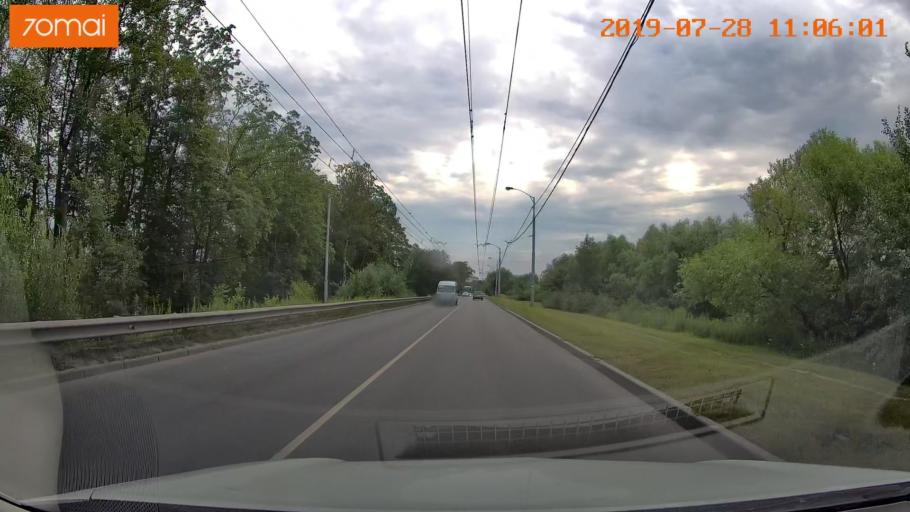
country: RU
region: Kaliningrad
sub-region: Gorod Kaliningrad
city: Kaliningrad
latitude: 54.7158
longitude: 20.4029
